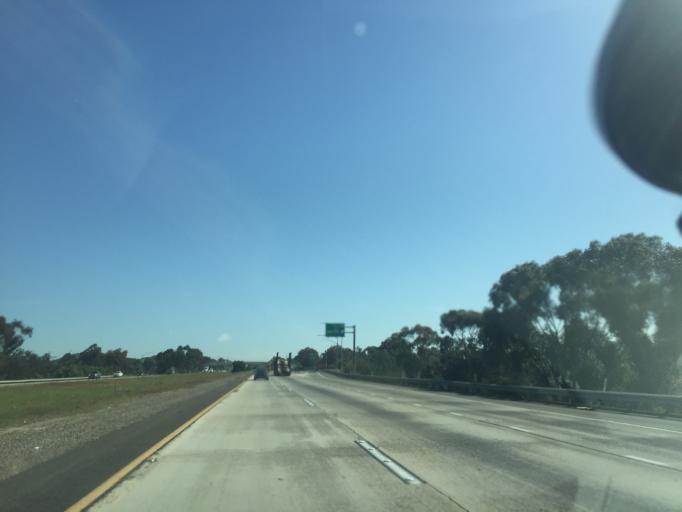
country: US
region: California
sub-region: San Diego County
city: Imperial Beach
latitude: 32.5681
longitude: -117.0476
